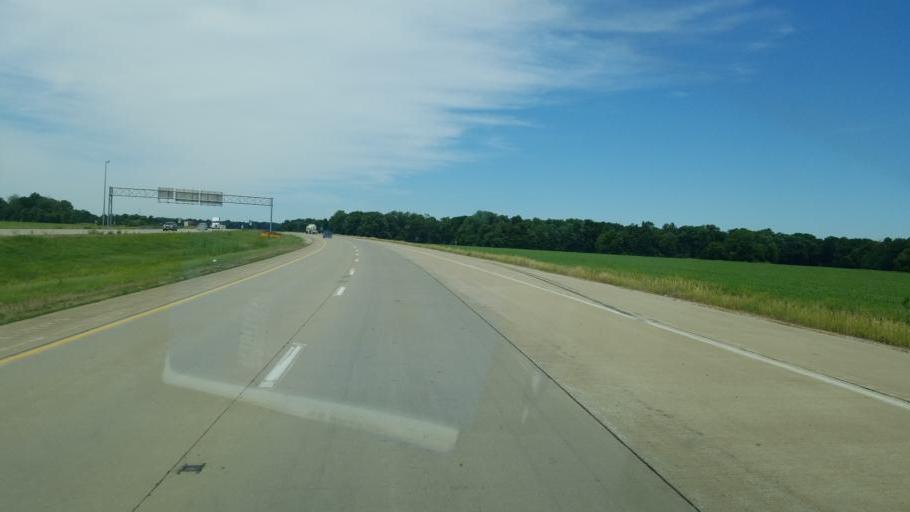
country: US
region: Indiana
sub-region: Vigo County
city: West Terre Haute
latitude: 39.4288
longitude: -87.5646
